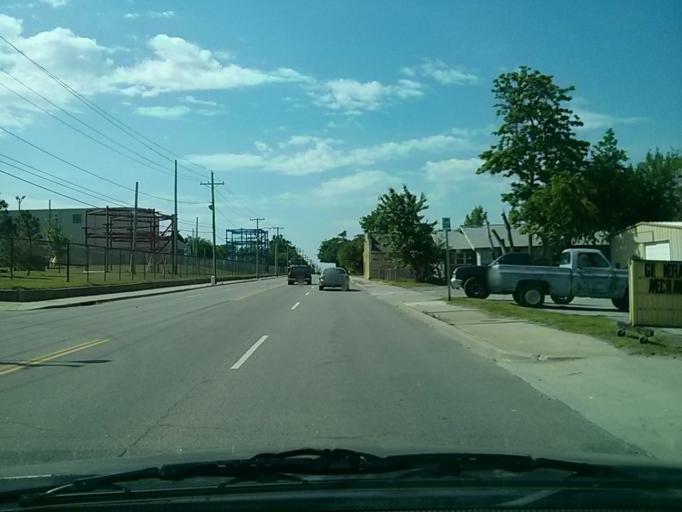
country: US
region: Oklahoma
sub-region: Tulsa County
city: Tulsa
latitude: 36.1690
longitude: -95.9757
